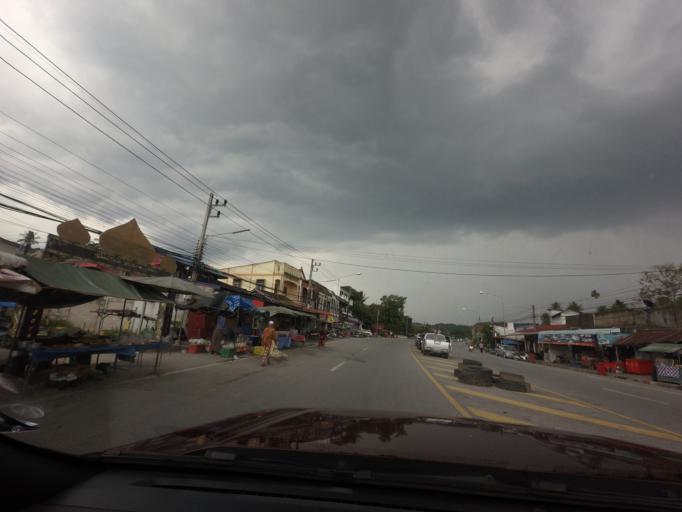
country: TH
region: Yala
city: Krong Pi Nang
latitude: 6.4141
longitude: 101.2800
